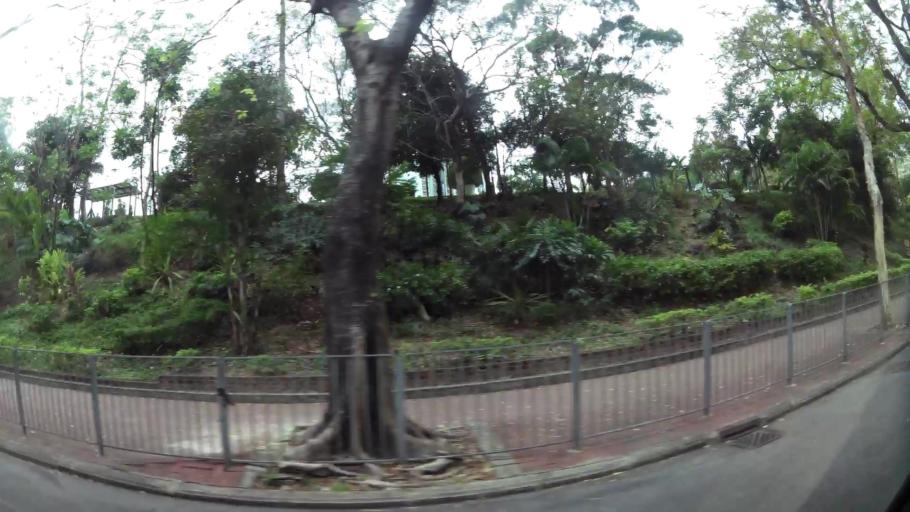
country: HK
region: Wong Tai Sin
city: Wong Tai Sin
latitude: 22.3363
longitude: 114.1915
